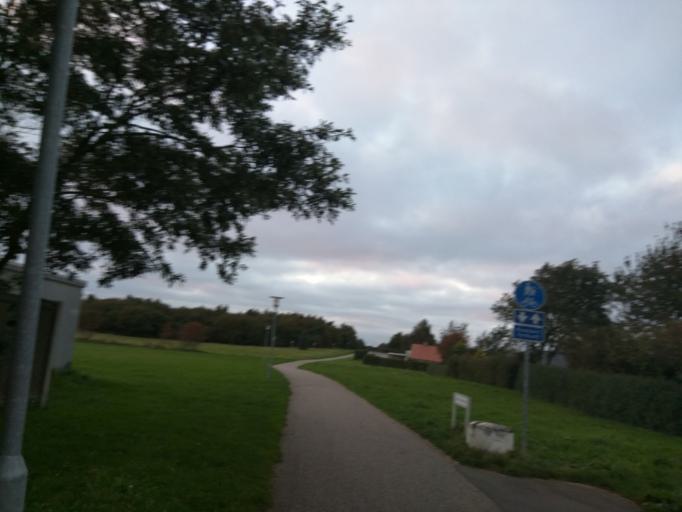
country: DK
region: Central Jutland
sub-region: Viborg Kommune
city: Viborg
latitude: 56.4450
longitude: 9.3752
